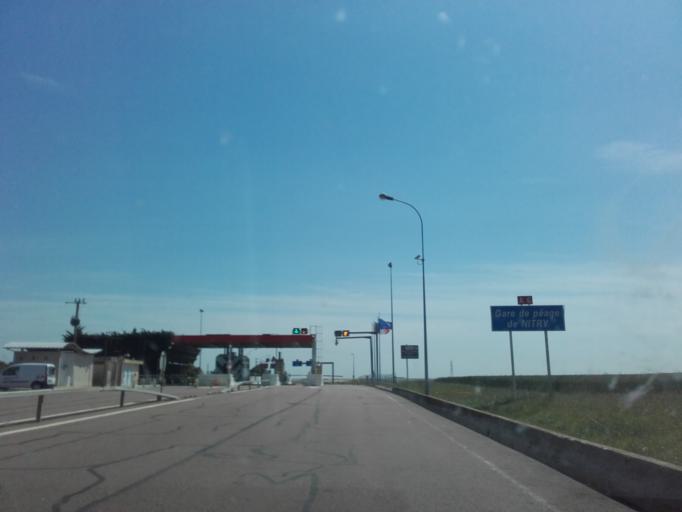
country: FR
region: Bourgogne
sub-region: Departement de l'Yonne
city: Joux-la-Ville
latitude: 47.6590
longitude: 3.8785
